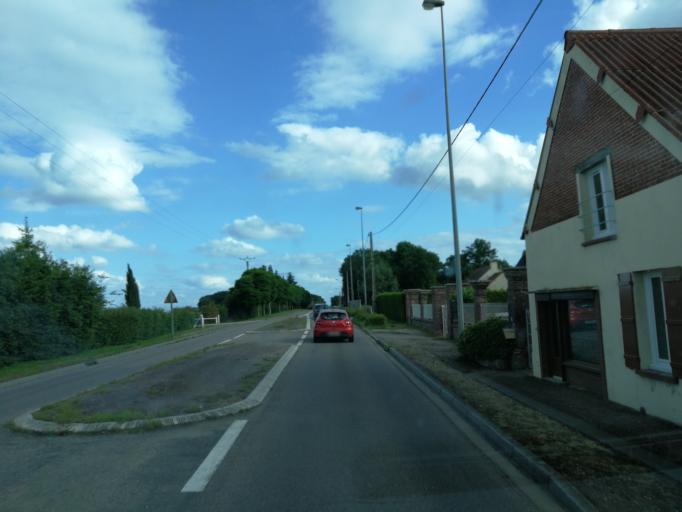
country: FR
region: Haute-Normandie
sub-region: Departement de l'Eure
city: Le Neubourg
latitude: 49.1189
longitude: 0.9111
